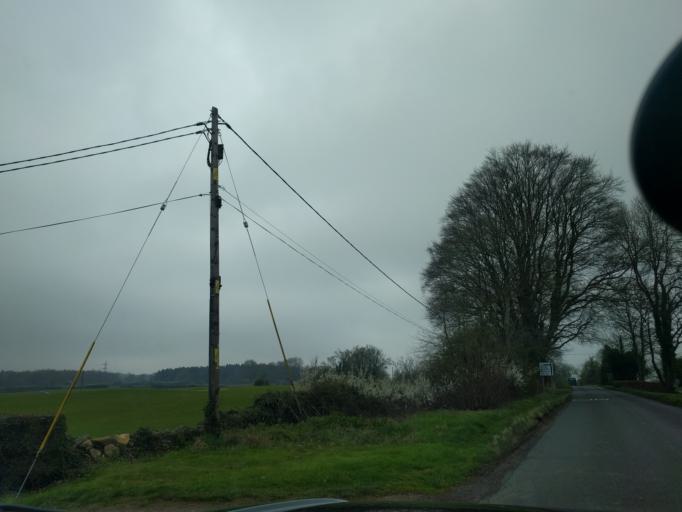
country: GB
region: England
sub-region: Wiltshire
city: Box
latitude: 51.4028
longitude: -2.2669
